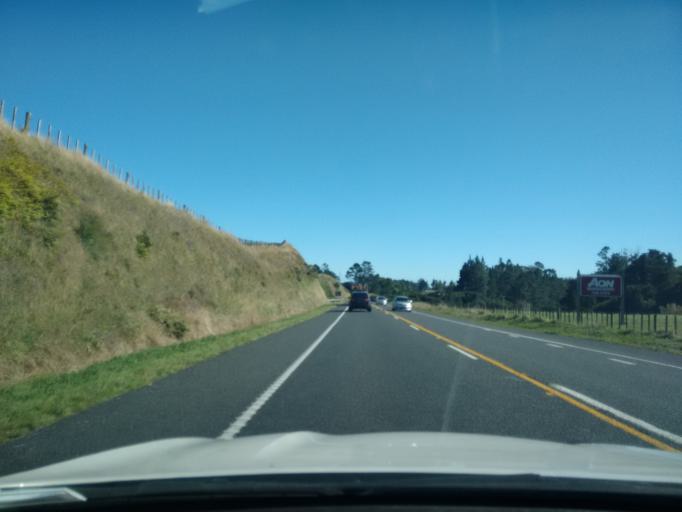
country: NZ
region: Taranaki
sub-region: New Plymouth District
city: New Plymouth
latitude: -39.1341
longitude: 174.1251
